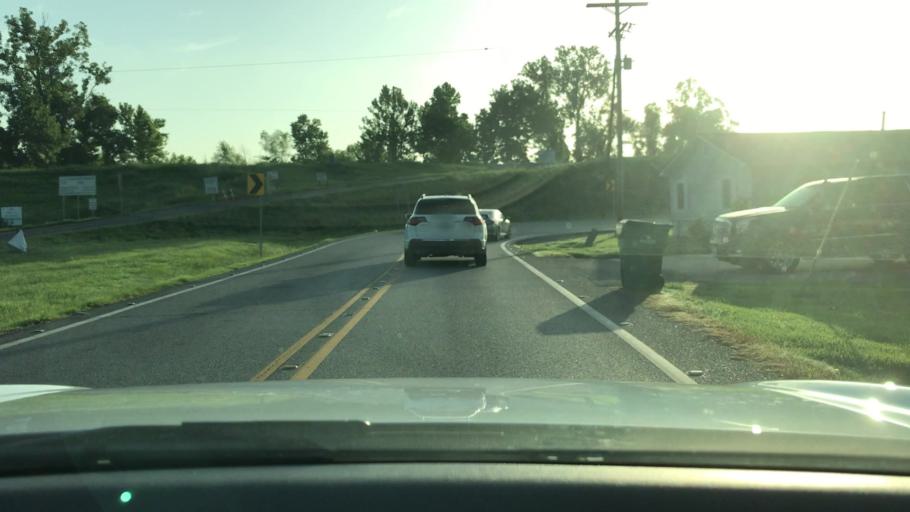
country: US
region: Louisiana
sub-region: Iberville Parish
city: Plaquemine
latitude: 30.2827
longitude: -91.2254
